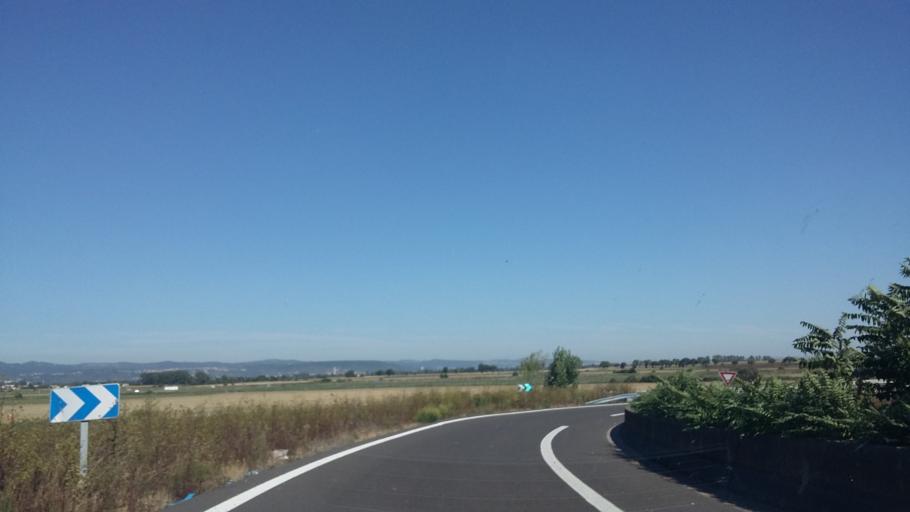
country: FR
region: Auvergne
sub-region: Departement du Puy-de-Dome
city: Malintrat
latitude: 45.7851
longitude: 3.1985
